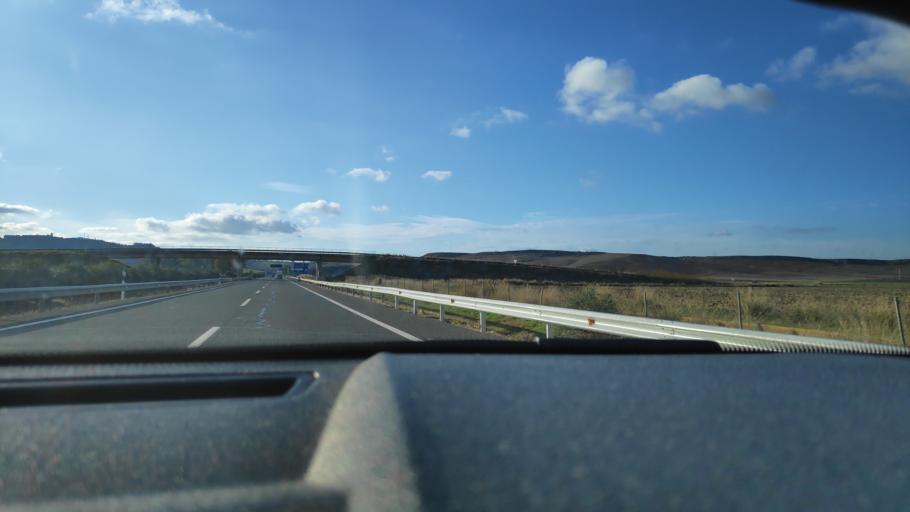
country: ES
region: Andalusia
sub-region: Provincia de Sevilla
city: Carmona
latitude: 37.4805
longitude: -5.5958
